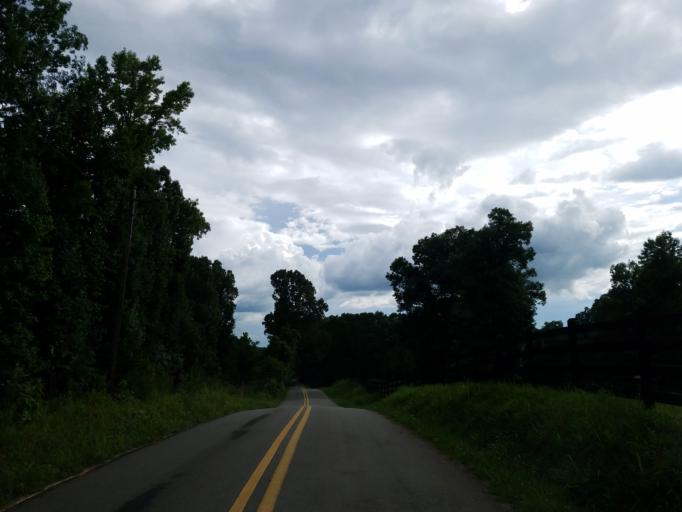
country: US
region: Georgia
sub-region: Pickens County
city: Jasper
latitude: 34.5431
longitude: -84.5301
